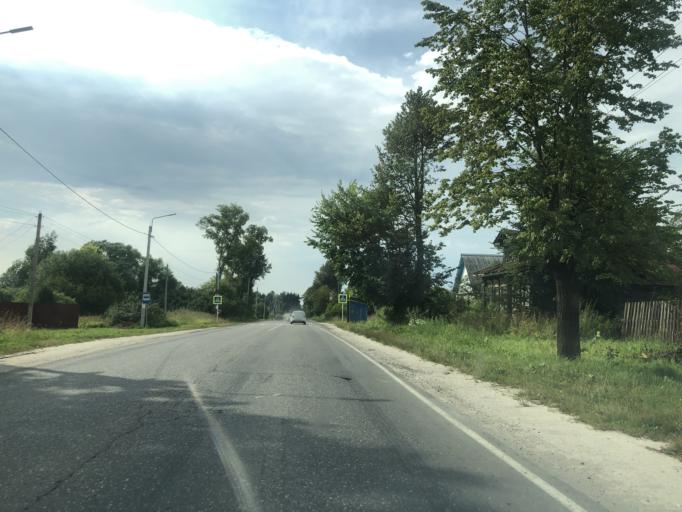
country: RU
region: Ivanovo
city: Shuya
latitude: 56.8572
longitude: 41.5070
